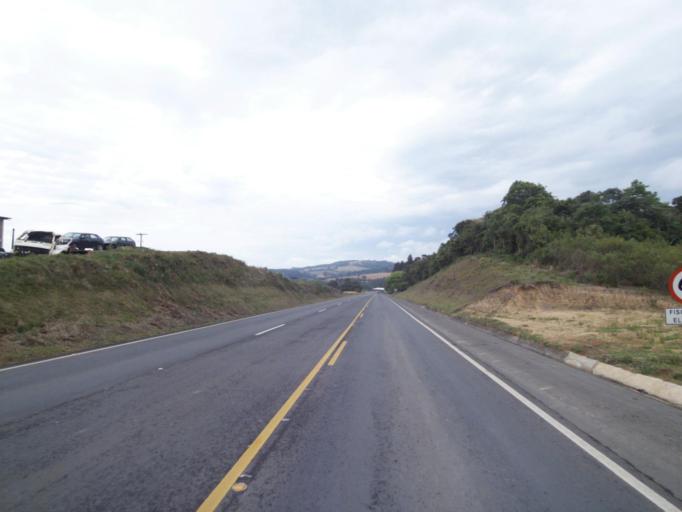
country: BR
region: Parana
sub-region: Irati
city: Irati
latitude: -25.4533
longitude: -50.6312
